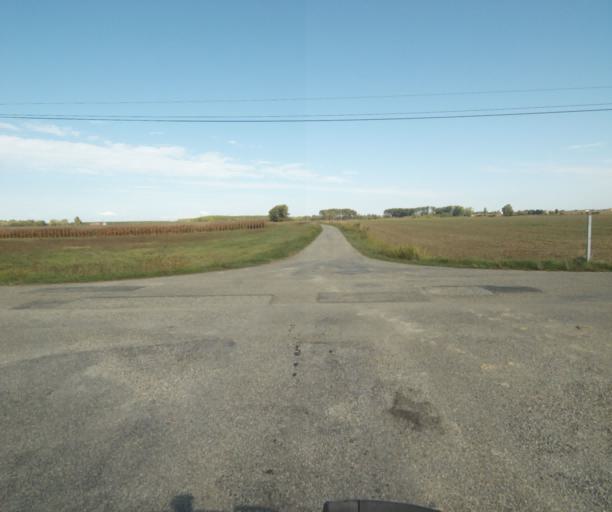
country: FR
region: Midi-Pyrenees
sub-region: Departement du Tarn-et-Garonne
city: Finhan
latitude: 43.8897
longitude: 1.2208
